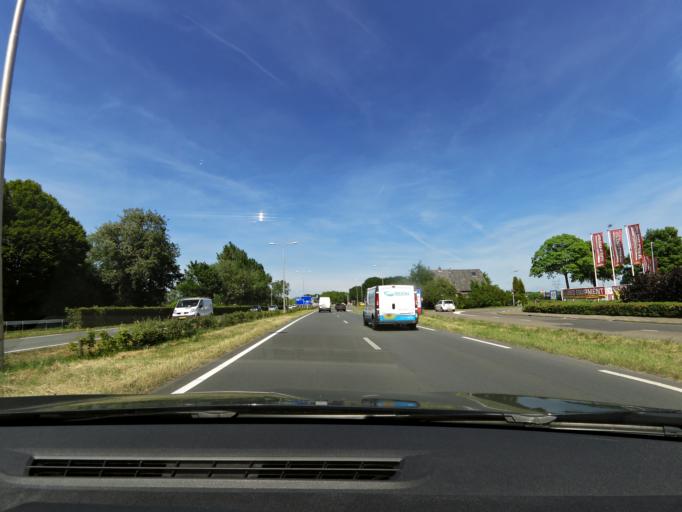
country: NL
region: South Holland
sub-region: Gemeente Albrandswaard
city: Rhoon
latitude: 51.8633
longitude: 4.4345
